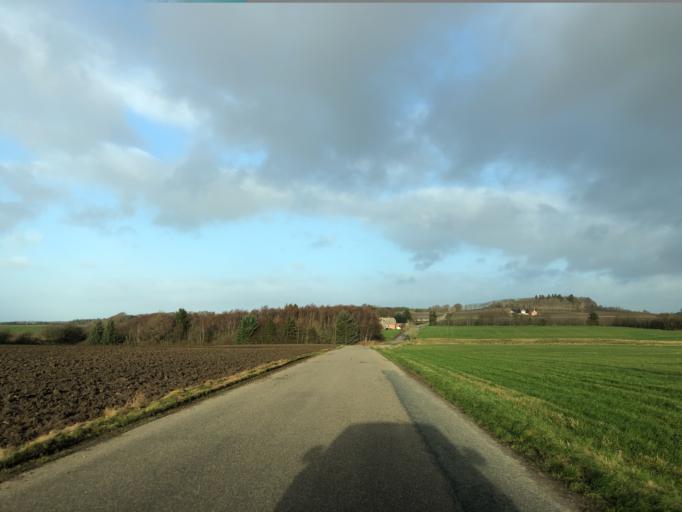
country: DK
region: Central Jutland
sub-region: Ringkobing-Skjern Kommune
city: Videbaek
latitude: 56.1799
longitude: 8.5391
